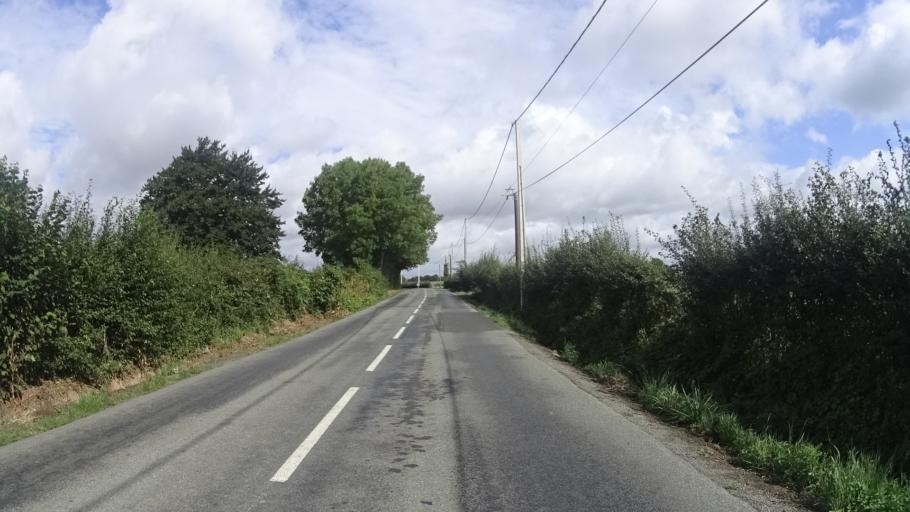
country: FR
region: Nord-Pas-de-Calais
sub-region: Departement du Nord
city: Landrecies
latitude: 50.0792
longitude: 3.6497
